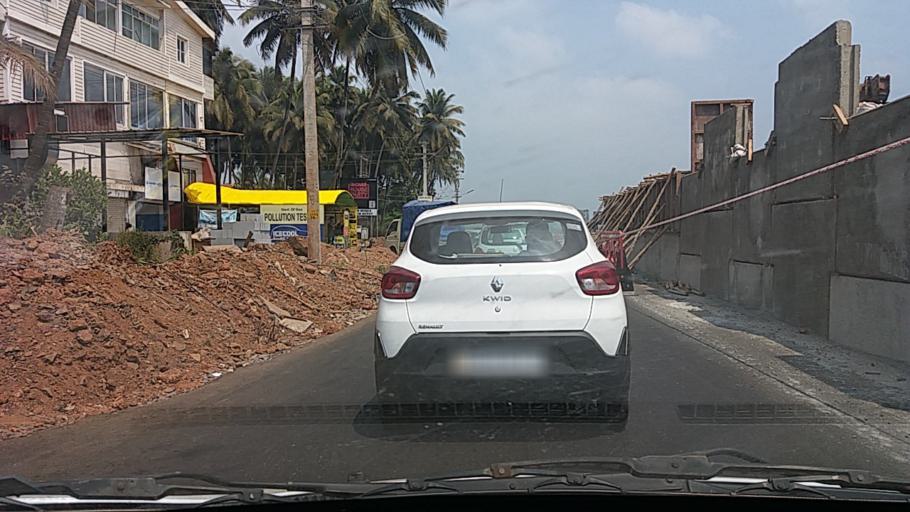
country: IN
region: Goa
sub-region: North Goa
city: Bambolim
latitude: 15.4729
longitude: 73.8501
